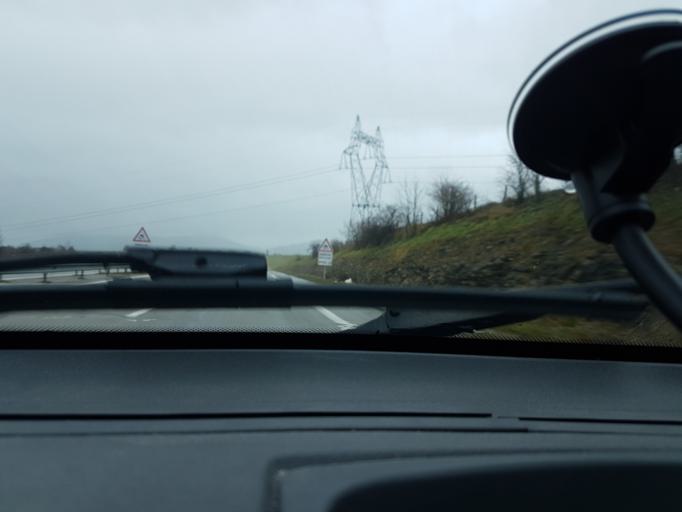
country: FR
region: Franche-Comte
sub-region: Departement du Doubs
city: Vercel-Villedieu-le-Camp
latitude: 47.1399
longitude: 6.4146
